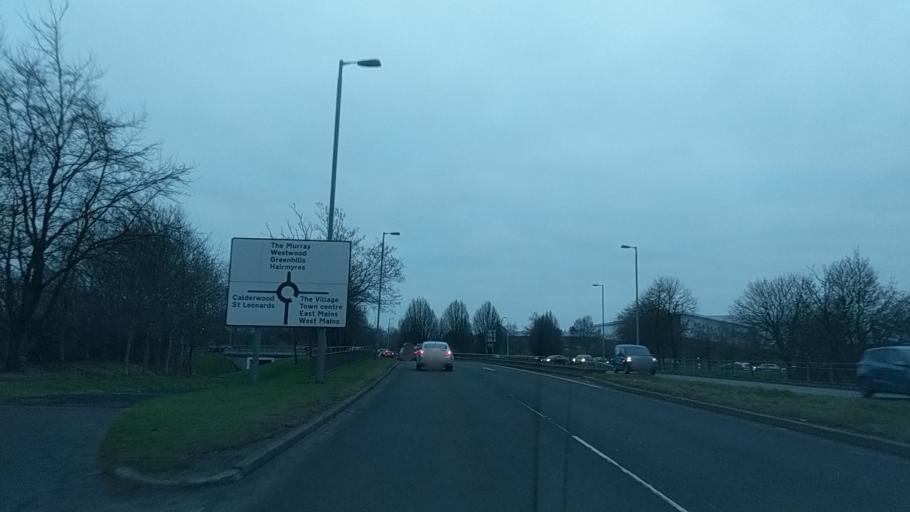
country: GB
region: Scotland
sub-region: South Lanarkshire
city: East Kilbride
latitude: 55.7644
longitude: -4.1660
